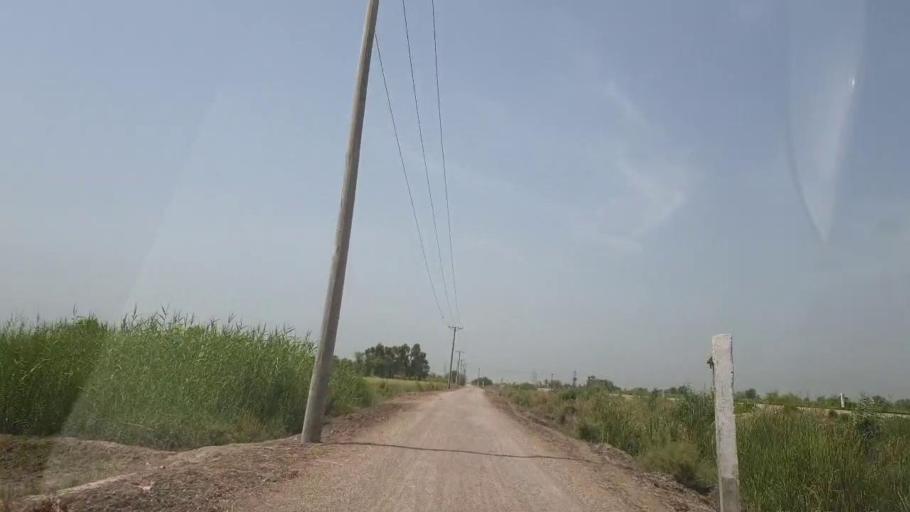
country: PK
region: Sindh
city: Gambat
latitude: 27.3229
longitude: 68.5375
